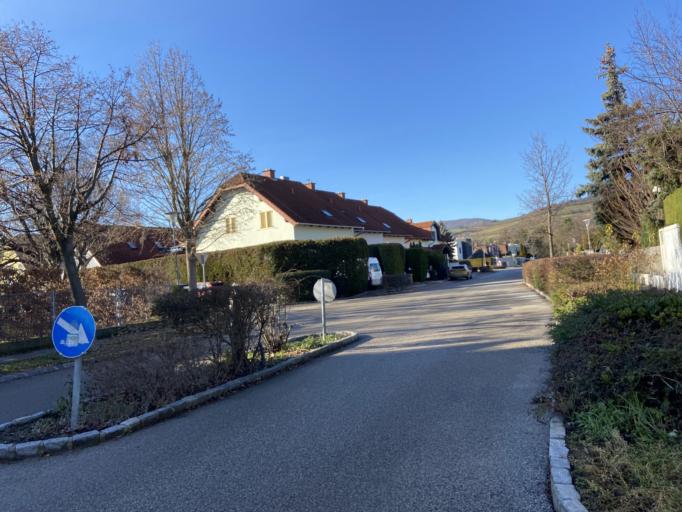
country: AT
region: Lower Austria
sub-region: Politischer Bezirk Modling
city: Neu-Guntramsdorf
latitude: 48.0595
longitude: 16.3153
